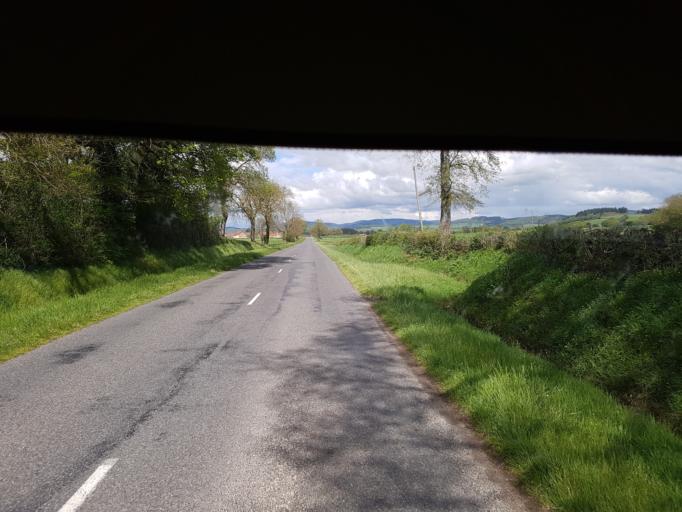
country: FR
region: Bourgogne
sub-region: Departement de Saone-et-Loire
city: Etang-sur-Arroux
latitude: 46.8123
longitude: 4.1602
